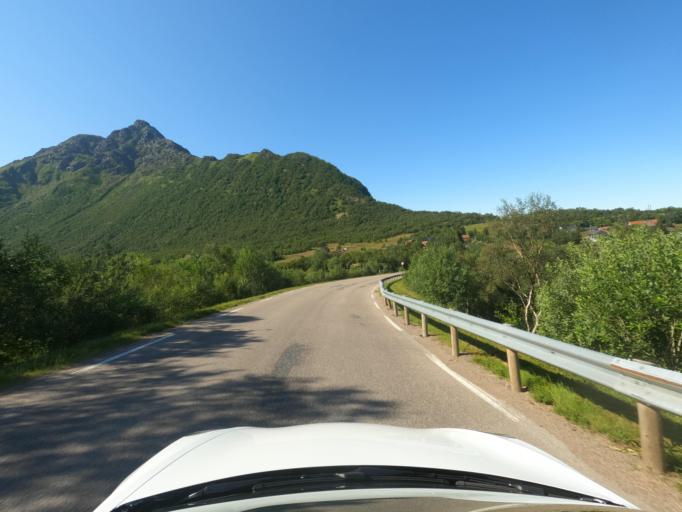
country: NO
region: Nordland
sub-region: Hadsel
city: Melbu
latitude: 68.4270
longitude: 14.8221
